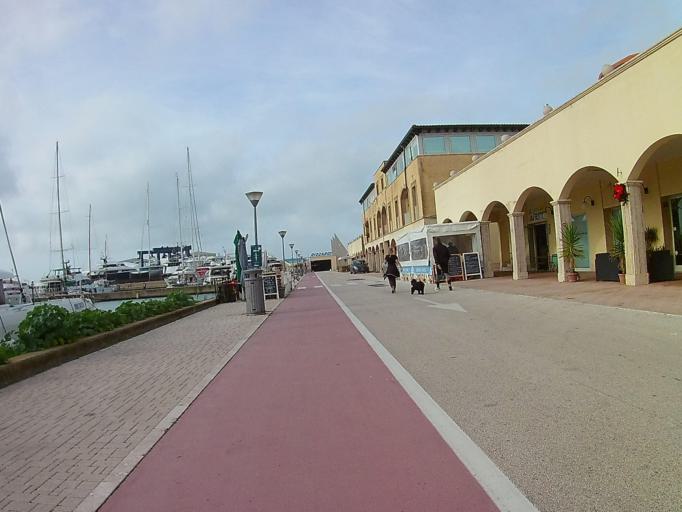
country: IT
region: Latium
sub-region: Citta metropolitana di Roma Capitale
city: Fiumicino-Isola Sacra
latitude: 41.7394
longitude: 12.2436
